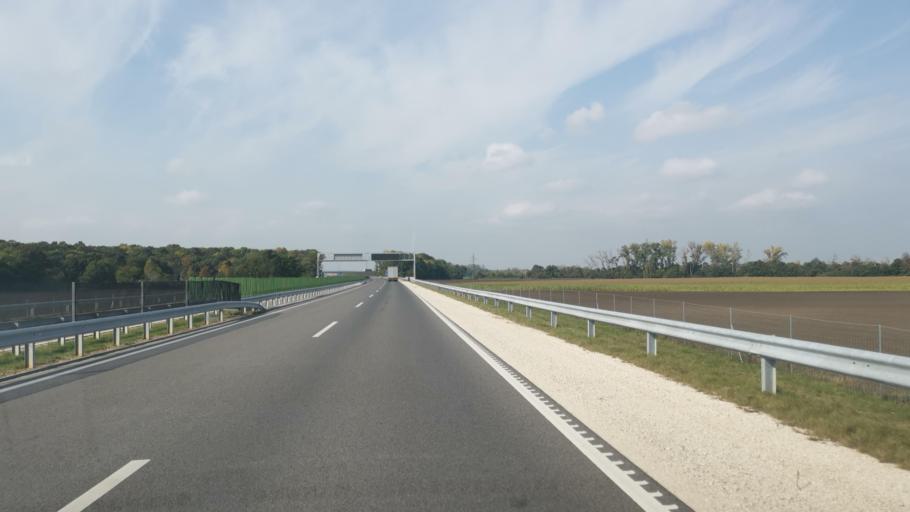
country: HU
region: Gyor-Moson-Sopron
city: Kapuvar
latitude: 47.5650
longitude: 17.0616
